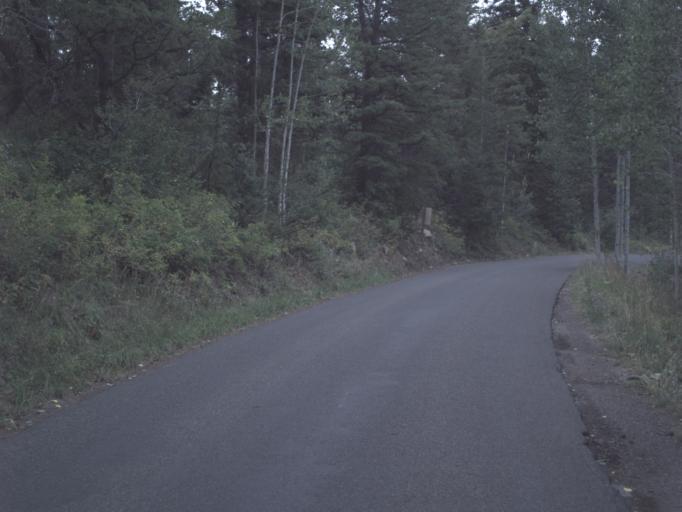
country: US
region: Utah
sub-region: Utah County
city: Lindon
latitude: 40.4352
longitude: -111.6308
